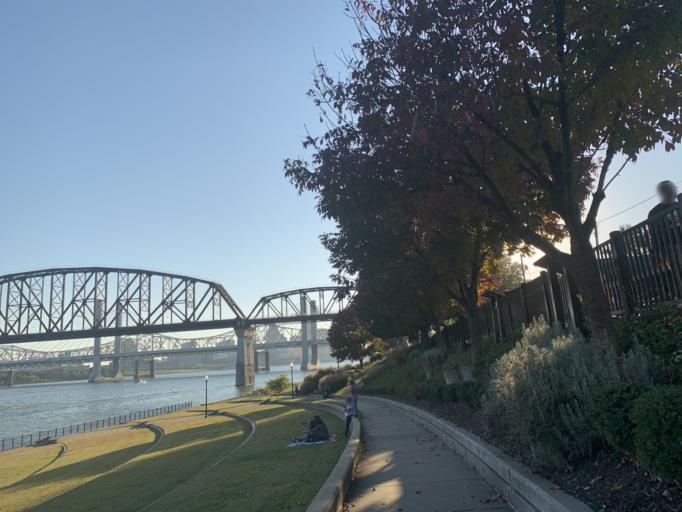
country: US
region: Indiana
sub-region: Clark County
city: Jeffersonville
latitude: 38.2693
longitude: -85.7391
